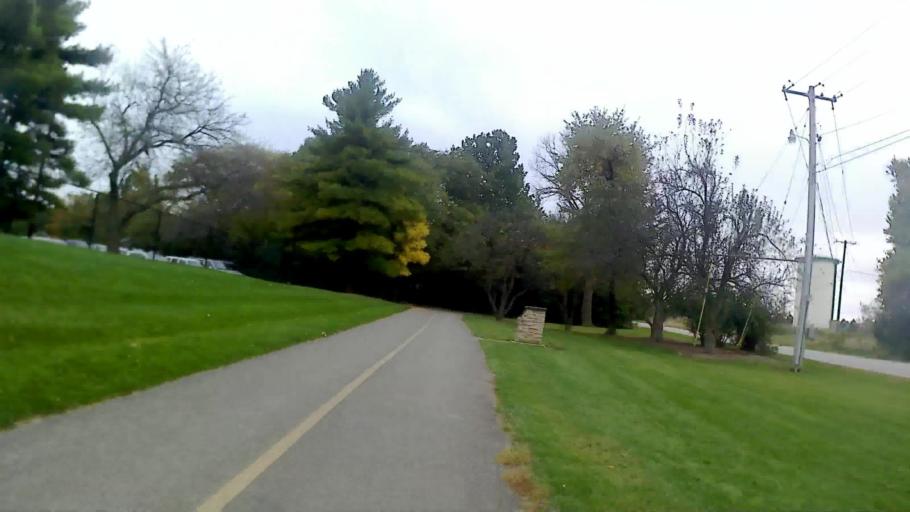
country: US
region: Illinois
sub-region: Kane County
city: Sugar Grove
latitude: 41.7637
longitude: -88.3914
